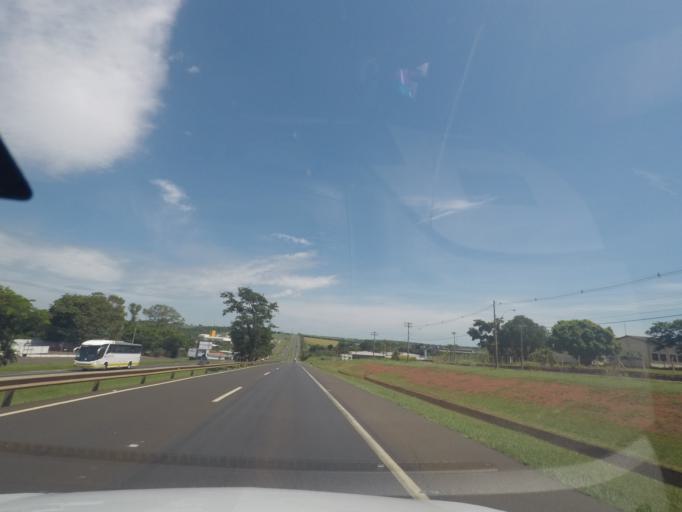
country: BR
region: Sao Paulo
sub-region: Araraquara
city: Araraquara
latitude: -21.7779
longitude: -48.2314
